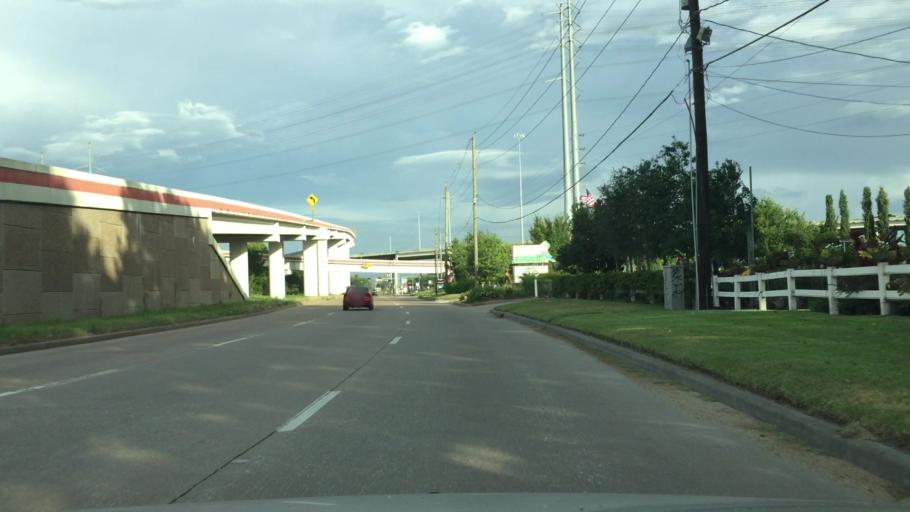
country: US
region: Texas
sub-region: Harris County
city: Hudson
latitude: 29.9393
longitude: -95.5201
